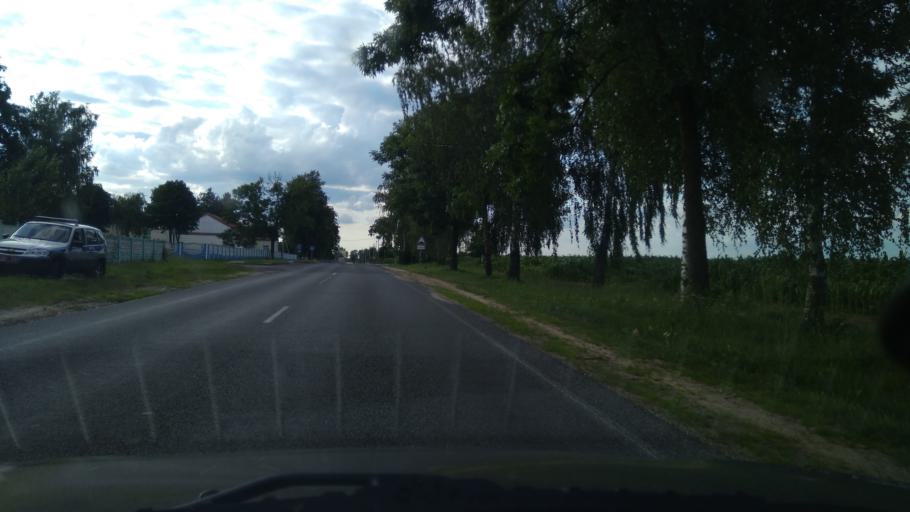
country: BY
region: Grodnenskaya
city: Masty
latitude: 53.3193
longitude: 24.6875
